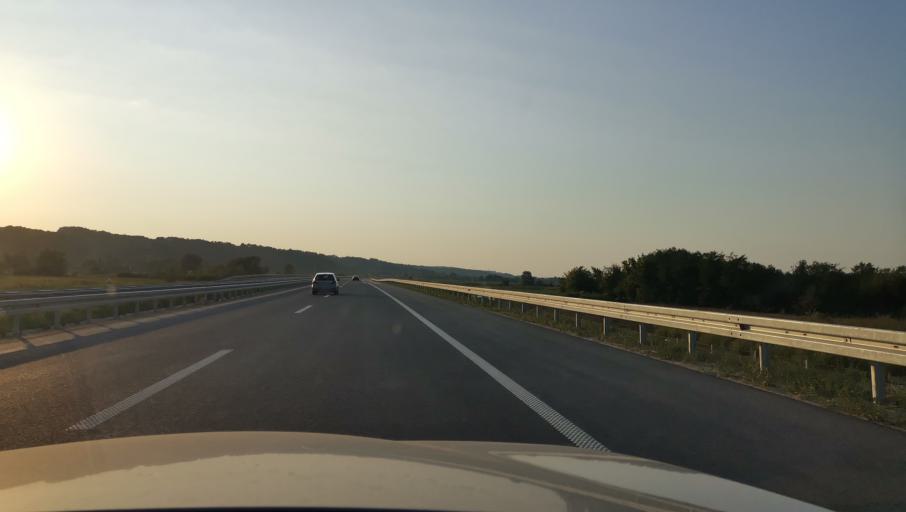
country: RS
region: Central Serbia
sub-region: Kolubarski Okrug
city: Ljig
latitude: 44.3086
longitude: 20.2247
